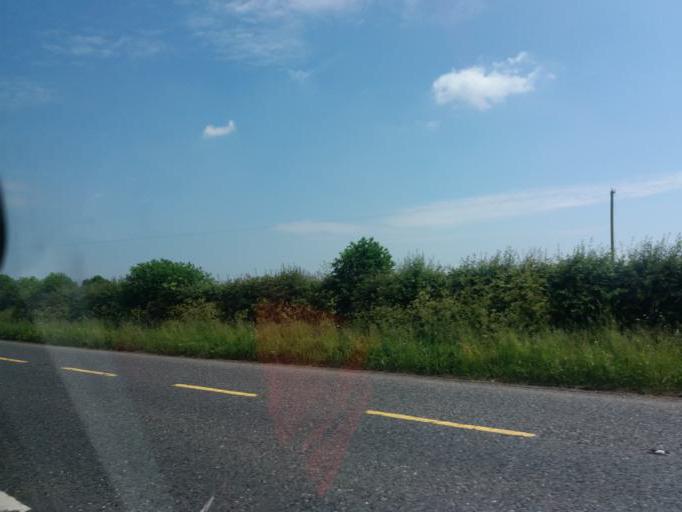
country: IE
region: Leinster
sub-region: An Mhi
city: Slane
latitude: 53.7041
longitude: -6.5793
